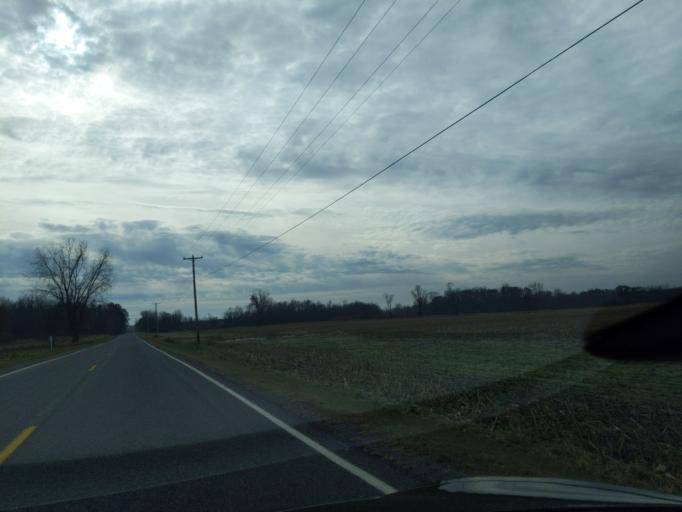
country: US
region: Michigan
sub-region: Ingham County
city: Leslie
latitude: 42.4895
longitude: -84.5217
